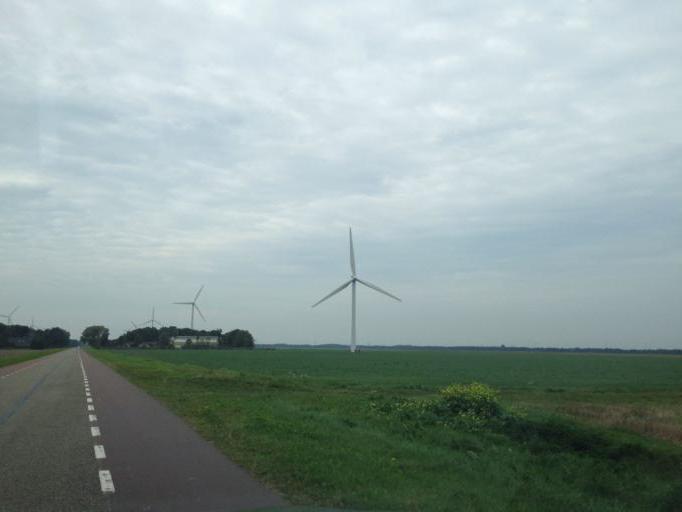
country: NL
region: Flevoland
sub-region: Gemeente Lelystad
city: Lelystad
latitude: 52.3959
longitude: 5.4320
